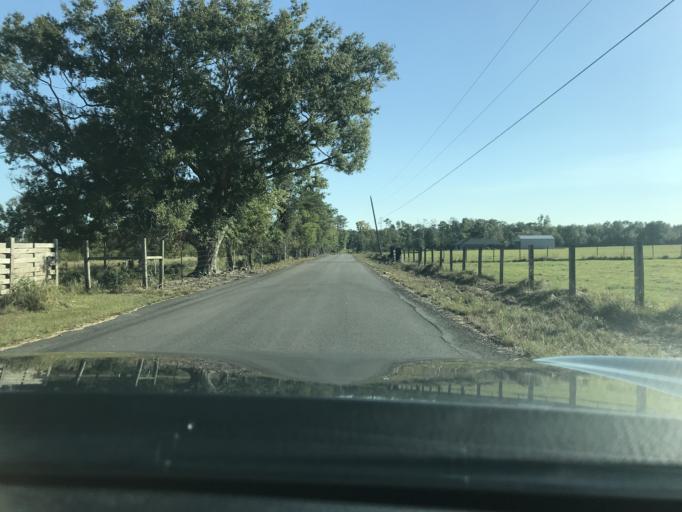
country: US
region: Louisiana
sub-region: Calcasieu Parish
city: Westlake
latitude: 30.3148
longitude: -93.2668
